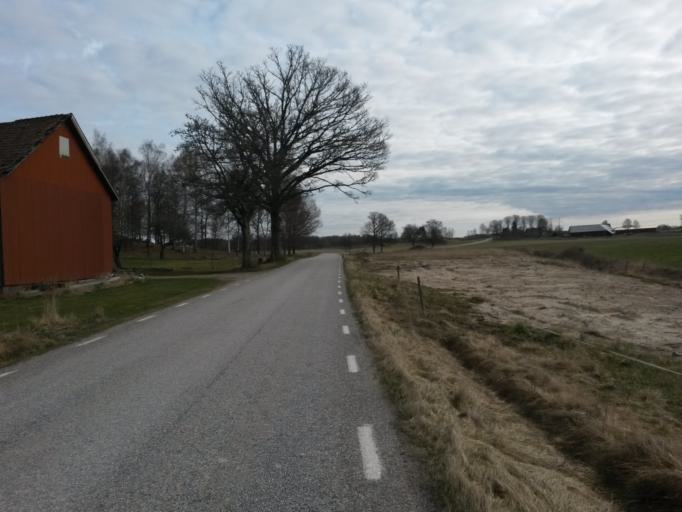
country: SE
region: Vaestra Goetaland
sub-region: Herrljunga Kommun
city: Herrljunga
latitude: 58.0886
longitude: 12.9354
